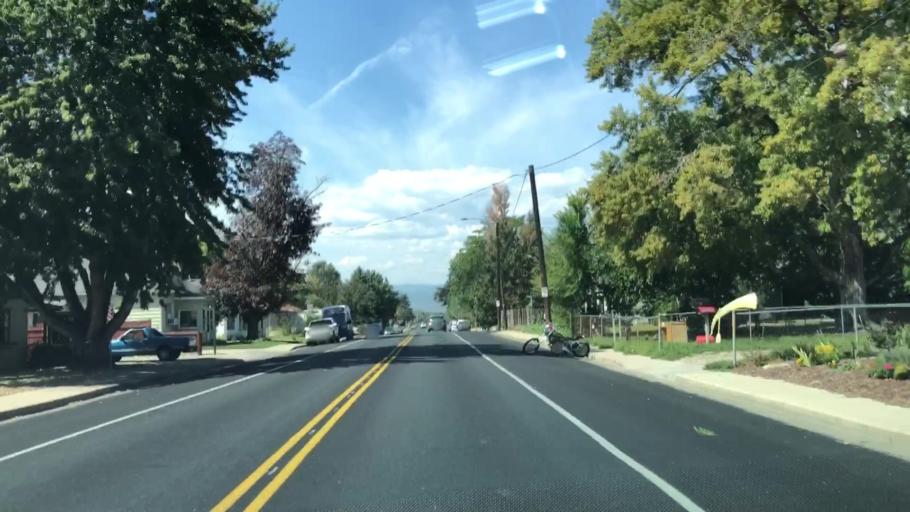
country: US
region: Colorado
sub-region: Larimer County
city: Loveland
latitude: 40.3928
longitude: -105.0829
